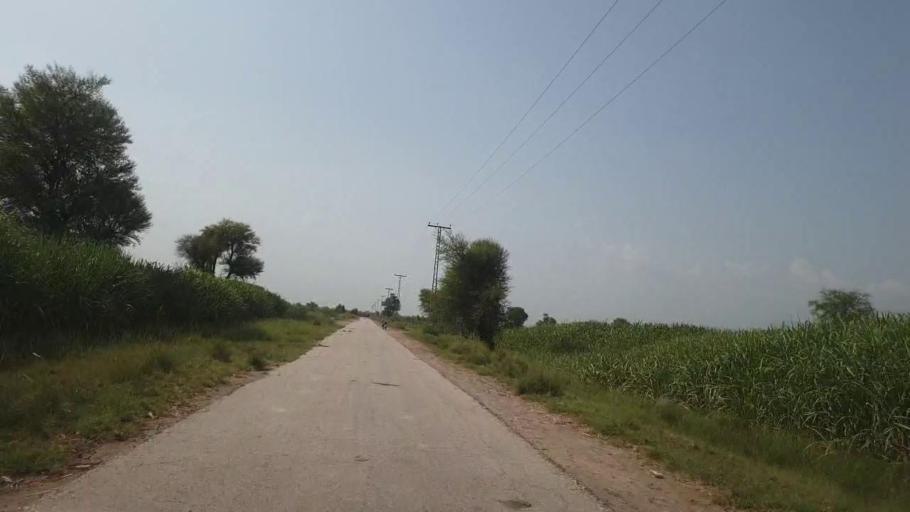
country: PK
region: Sindh
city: Pano Aqil
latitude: 27.7859
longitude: 69.1574
